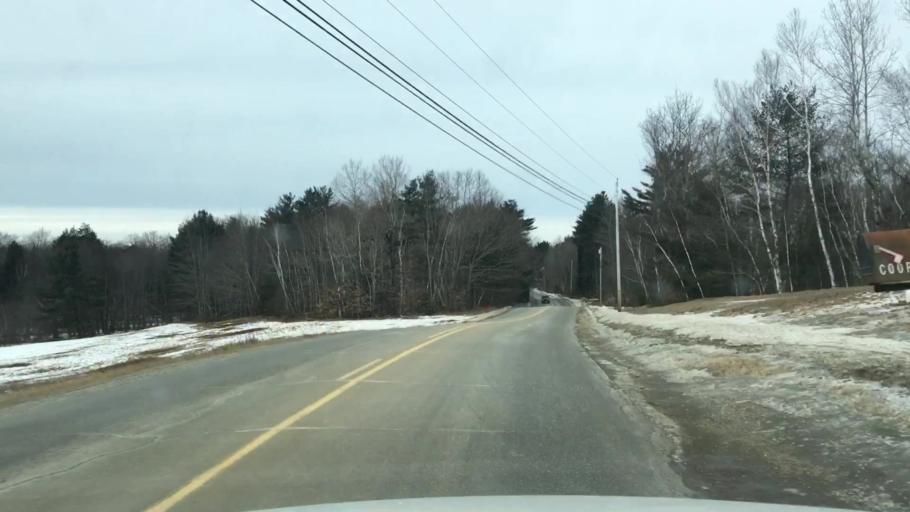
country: US
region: Maine
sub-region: Kennebec County
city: Chelsea
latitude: 44.2664
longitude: -69.6503
